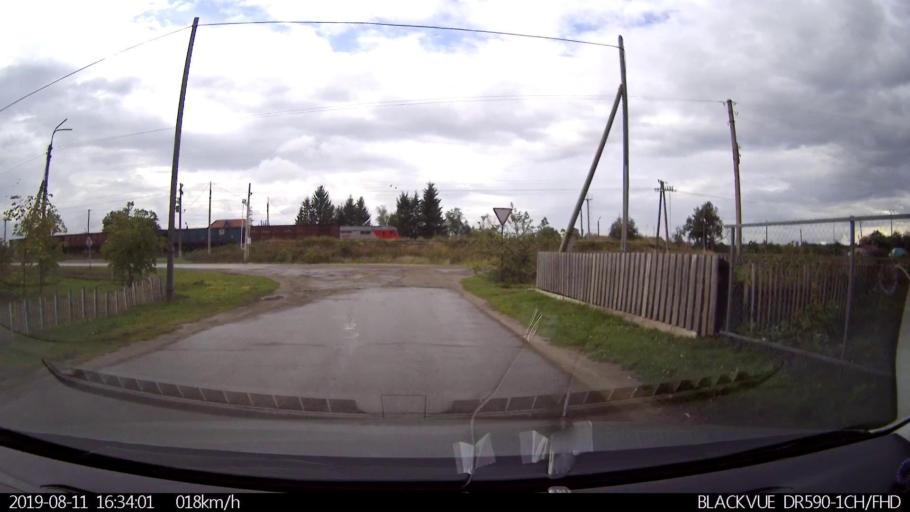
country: RU
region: Ulyanovsk
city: Mayna
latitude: 54.1165
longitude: 47.6236
